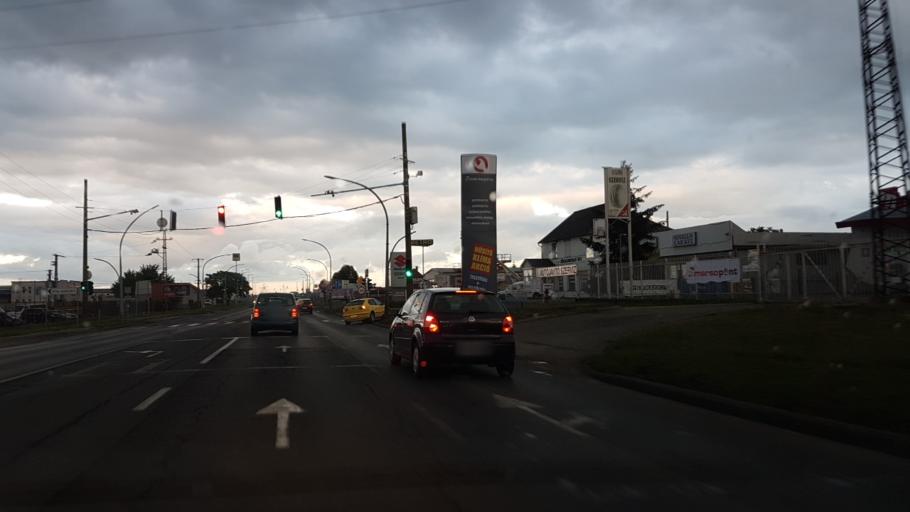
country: HU
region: Borsod-Abauj-Zemplen
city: Arnot
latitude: 48.1065
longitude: 20.8264
